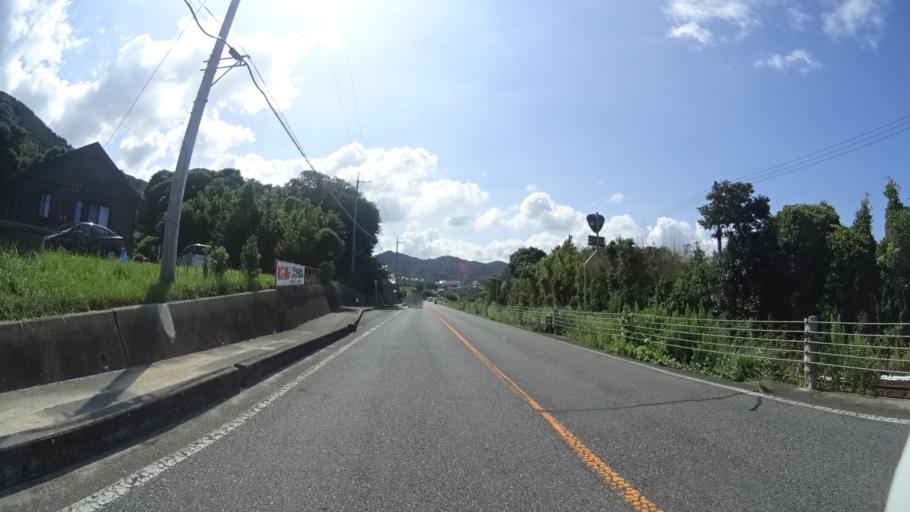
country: JP
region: Yamaguchi
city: Shimonoseki
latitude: 34.2130
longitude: 130.9315
